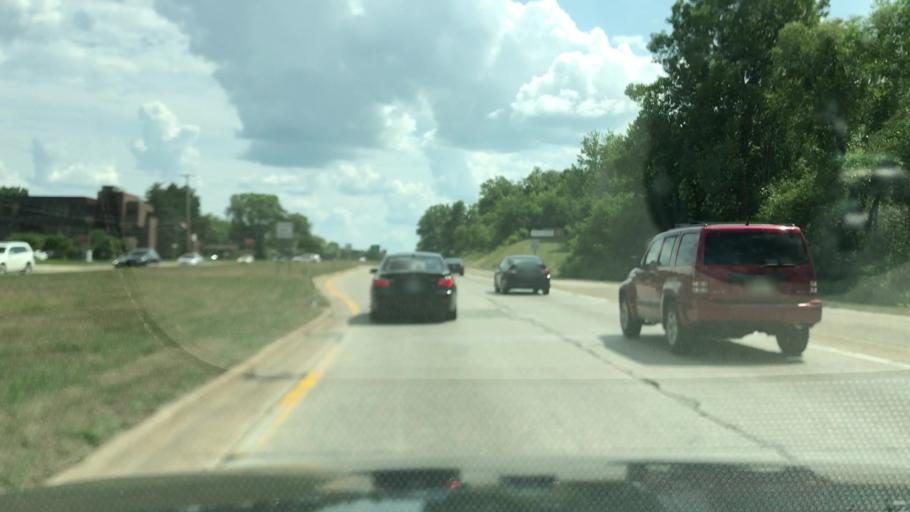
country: US
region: Michigan
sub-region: Kent County
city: East Grand Rapids
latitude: 42.9375
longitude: -85.5854
